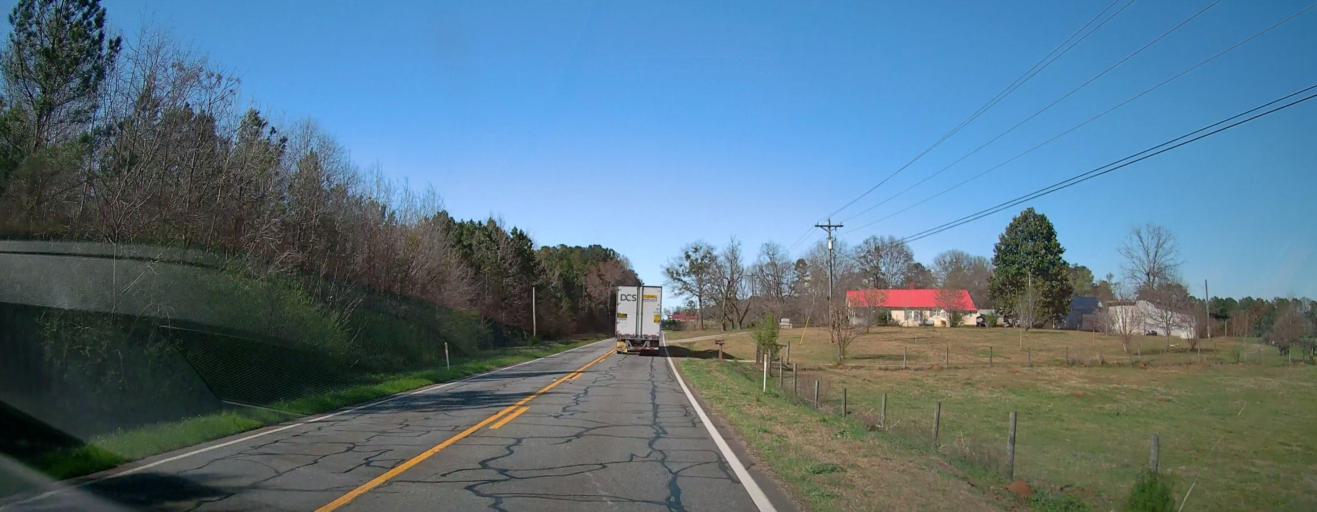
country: US
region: Georgia
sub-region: Butts County
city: Indian Springs
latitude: 33.1705
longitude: -83.9582
